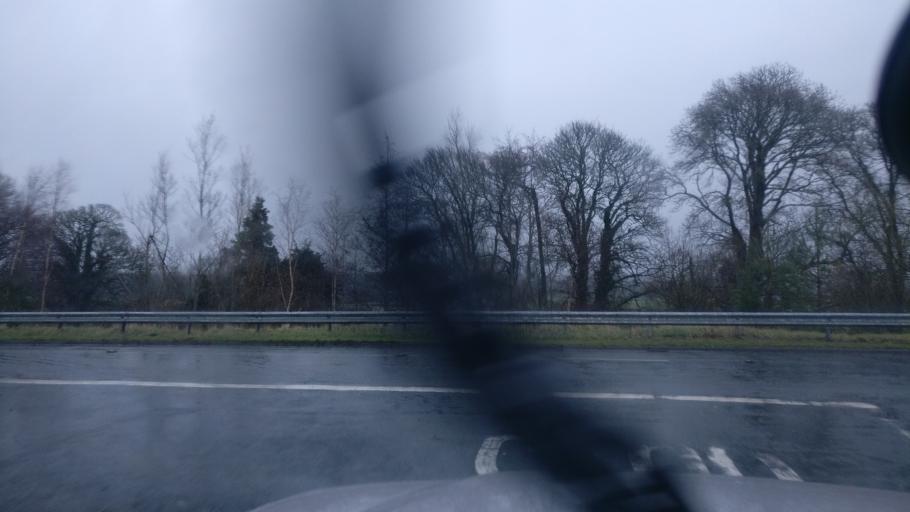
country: IE
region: Connaught
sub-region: County Galway
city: Ballinasloe
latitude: 53.3077
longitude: -8.3219
